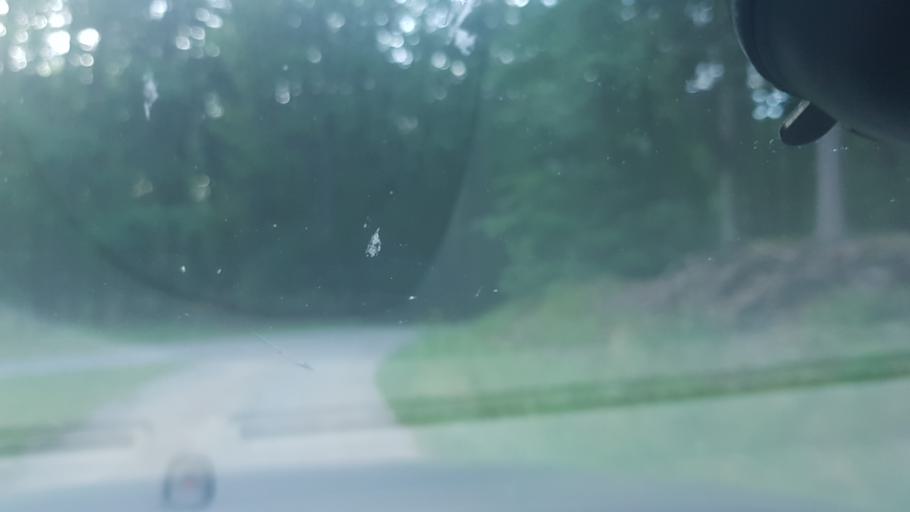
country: PL
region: Pomeranian Voivodeship
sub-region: Powiat nowodworski
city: Krynica Morska
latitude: 54.3548
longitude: 19.3435
